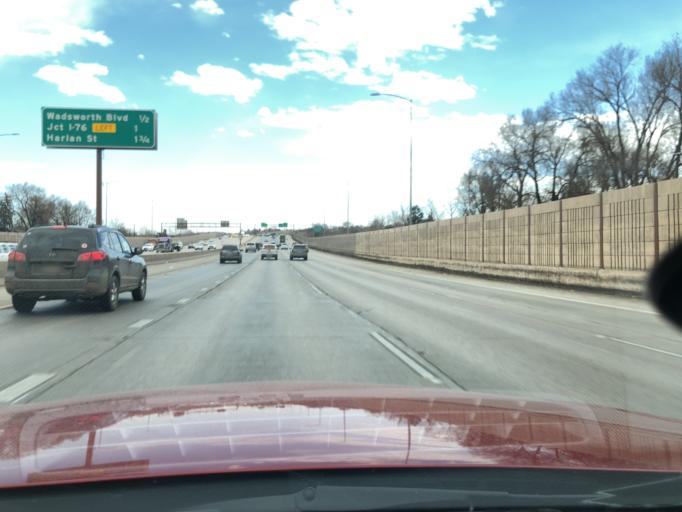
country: US
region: Colorado
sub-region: Jefferson County
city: Arvada
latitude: 39.7834
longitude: -105.0976
